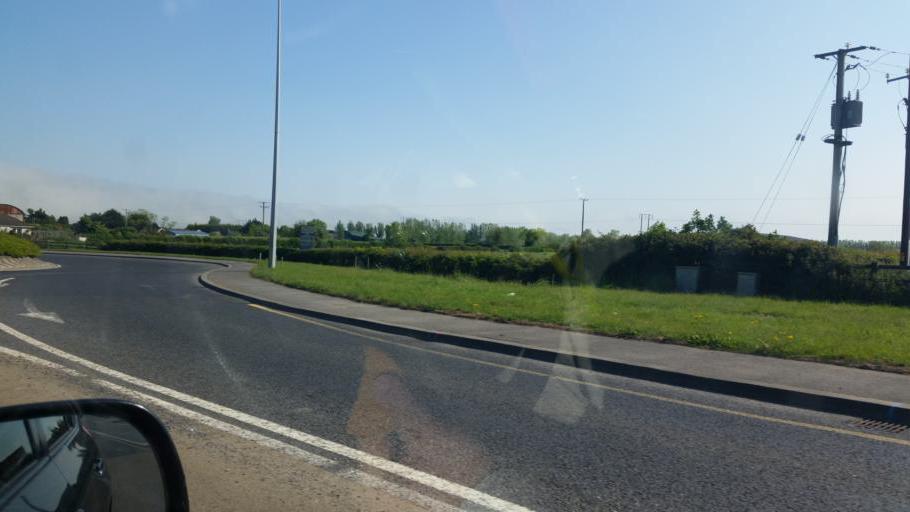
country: IE
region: Leinster
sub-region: Dublin City
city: Finglas
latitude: 53.4341
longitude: -6.3336
